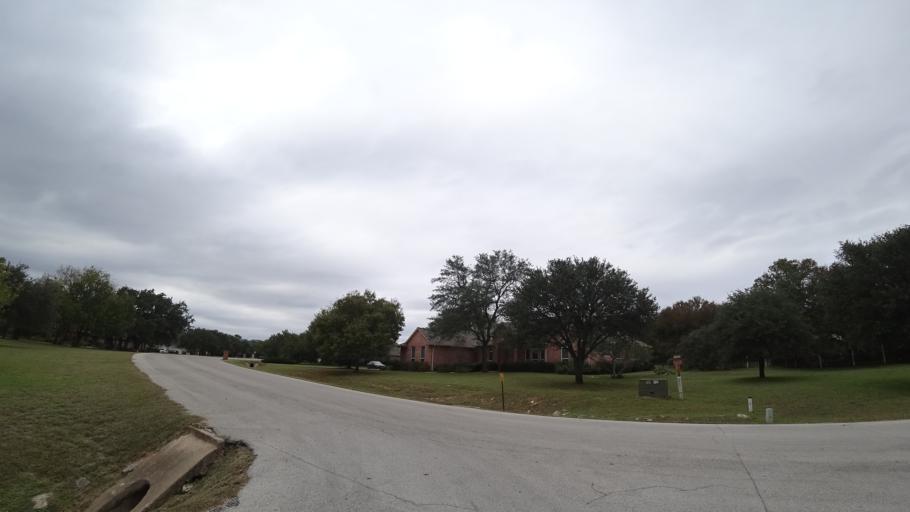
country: US
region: Texas
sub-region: Travis County
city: Shady Hollow
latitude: 30.1546
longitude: -97.8712
